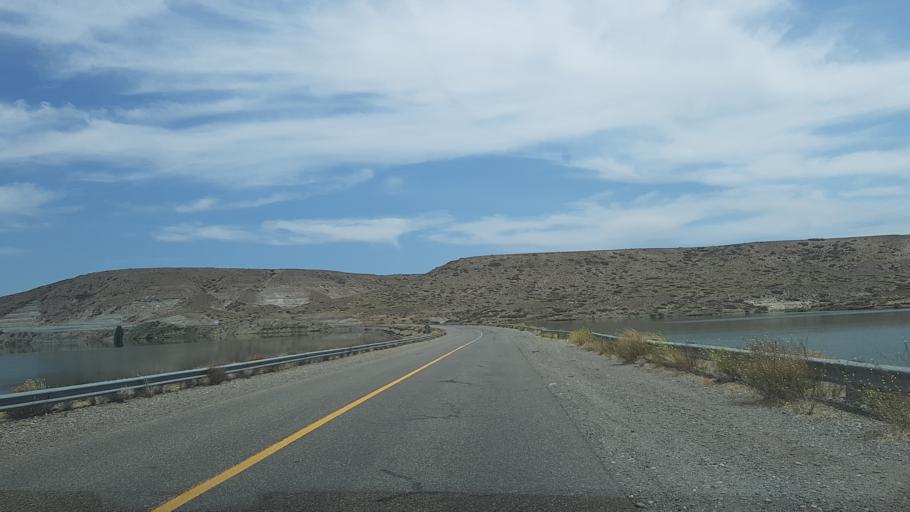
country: AR
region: Neuquen
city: Junin de los Andes
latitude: -40.4373
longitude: -70.6532
